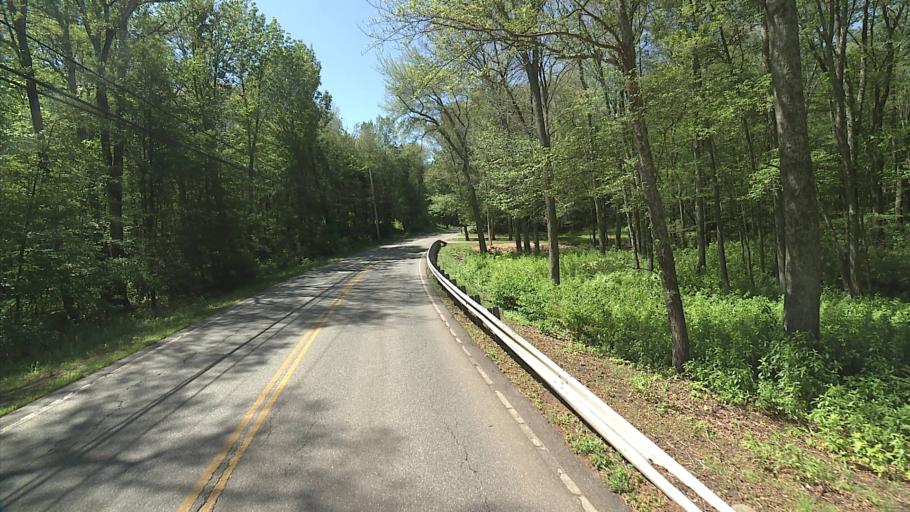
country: US
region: Connecticut
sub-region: New London County
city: Colchester
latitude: 41.5911
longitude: -72.3043
